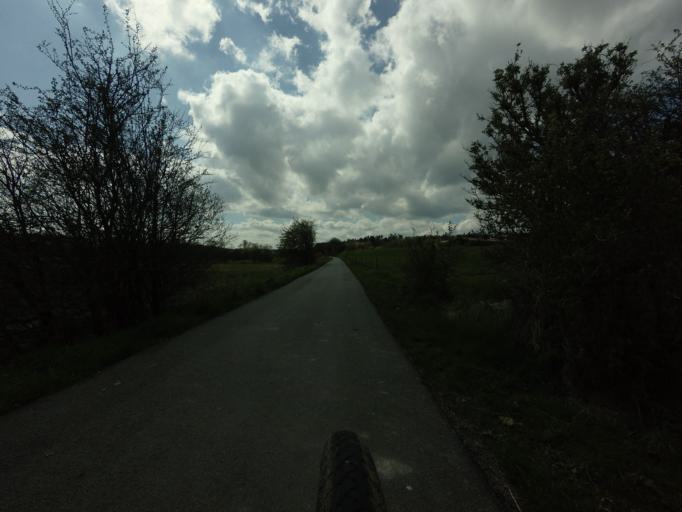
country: DK
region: North Denmark
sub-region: Alborg Kommune
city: Storvorde
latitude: 56.8620
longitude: 10.1085
